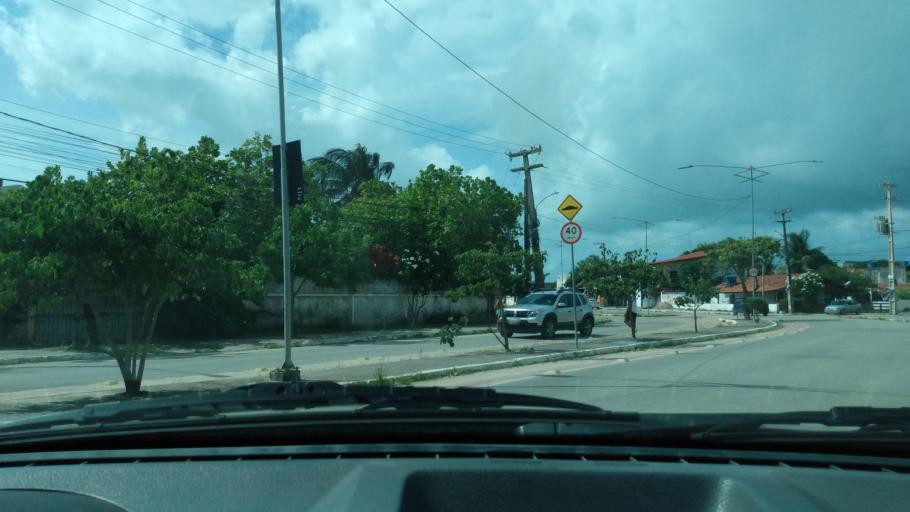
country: BR
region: Pernambuco
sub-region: Cabo De Santo Agostinho
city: Cabo
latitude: -8.3212
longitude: -34.9529
